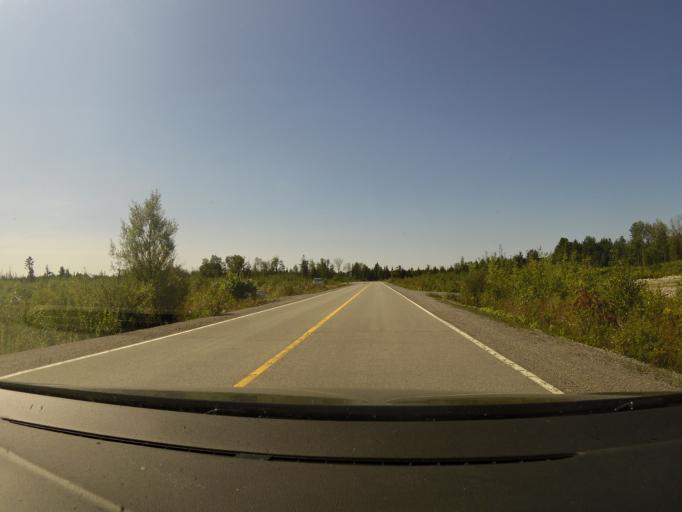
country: CA
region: Ontario
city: Bells Corners
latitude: 45.2530
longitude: -75.9744
